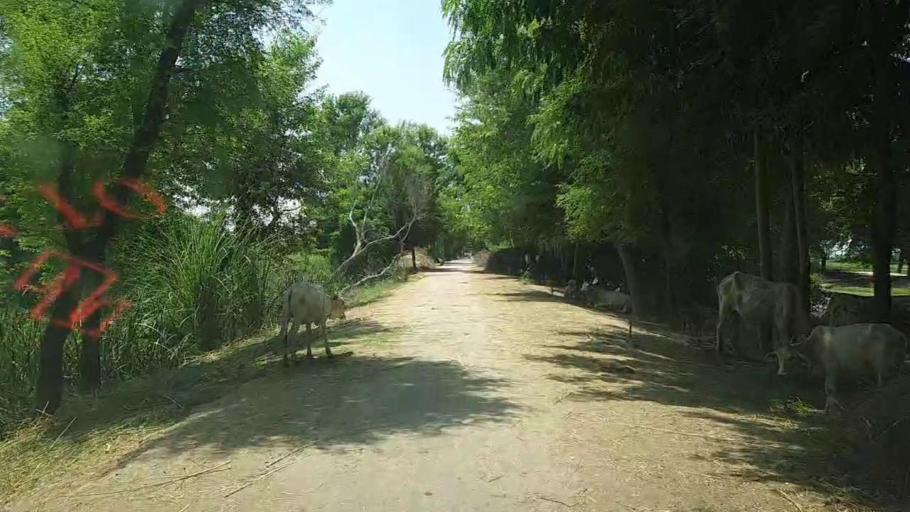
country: PK
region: Sindh
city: Ubauro
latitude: 28.1471
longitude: 69.7767
